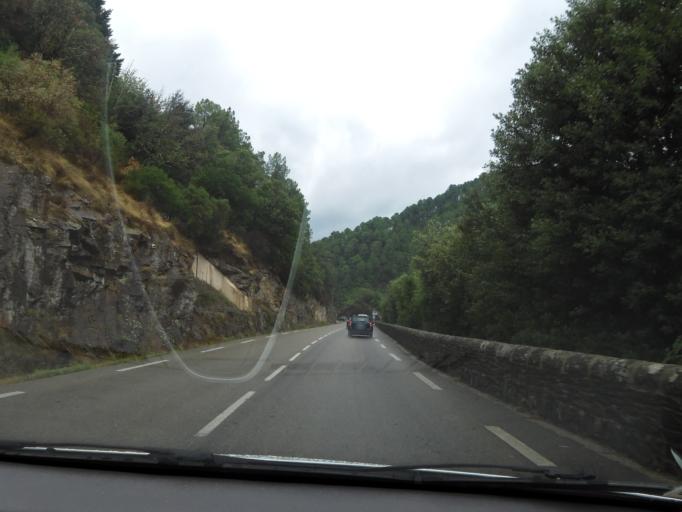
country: FR
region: Languedoc-Roussillon
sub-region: Departement du Gard
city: Branoux-les-Taillades
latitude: 44.2503
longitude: 3.9735
